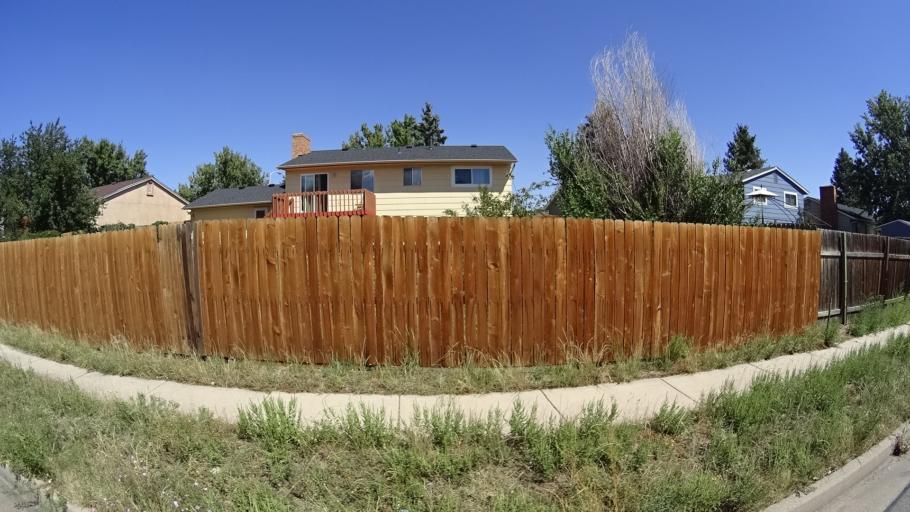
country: US
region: Colorado
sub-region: El Paso County
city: Stratmoor
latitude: 38.7929
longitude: -104.7417
